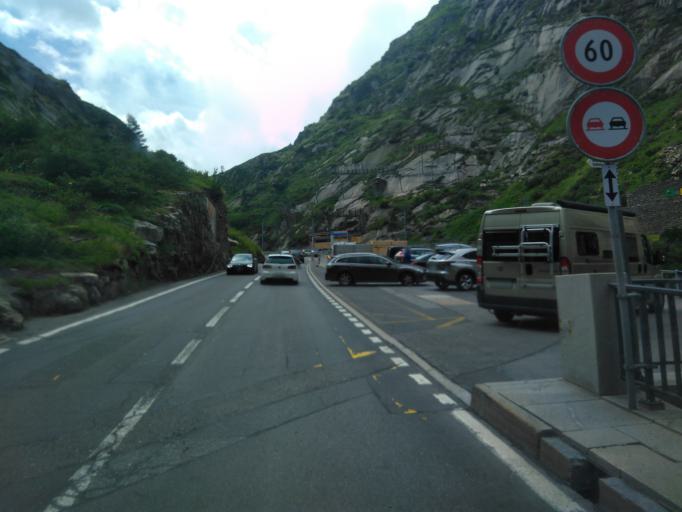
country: CH
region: Uri
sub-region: Uri
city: Andermatt
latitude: 46.6469
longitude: 8.5900
